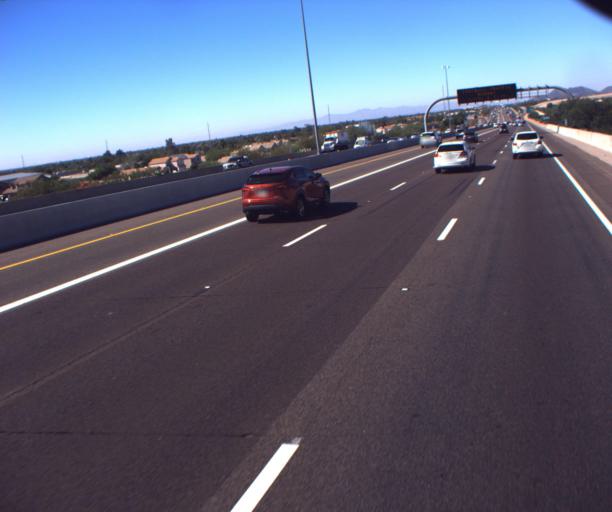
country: US
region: Arizona
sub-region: Maricopa County
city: Paradise Valley
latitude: 33.6692
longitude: -112.0505
